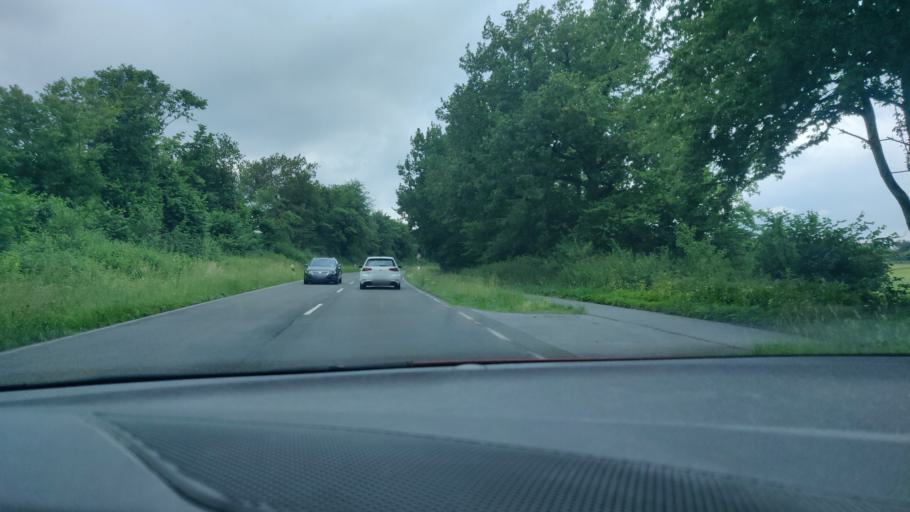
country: DE
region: North Rhine-Westphalia
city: Wulfrath
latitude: 51.2929
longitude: 7.0891
